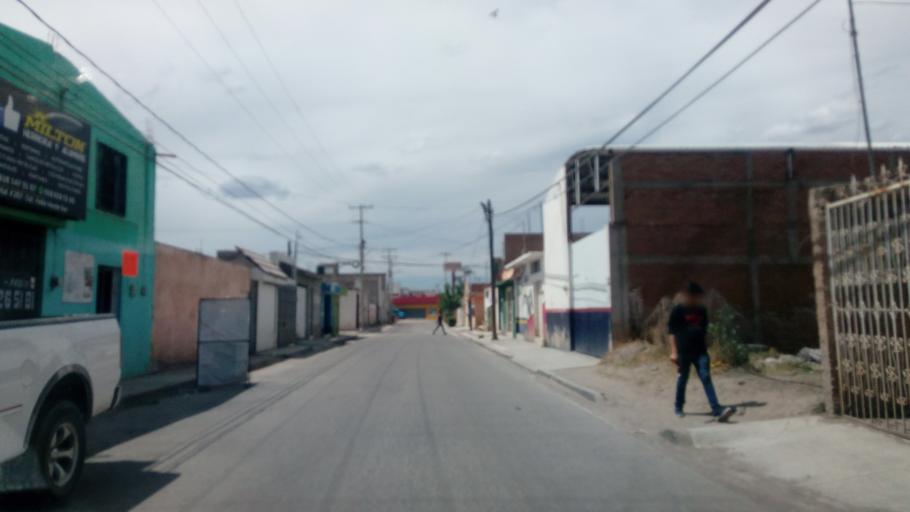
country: MX
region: Durango
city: Victoria de Durango
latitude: 23.9939
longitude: -104.6466
